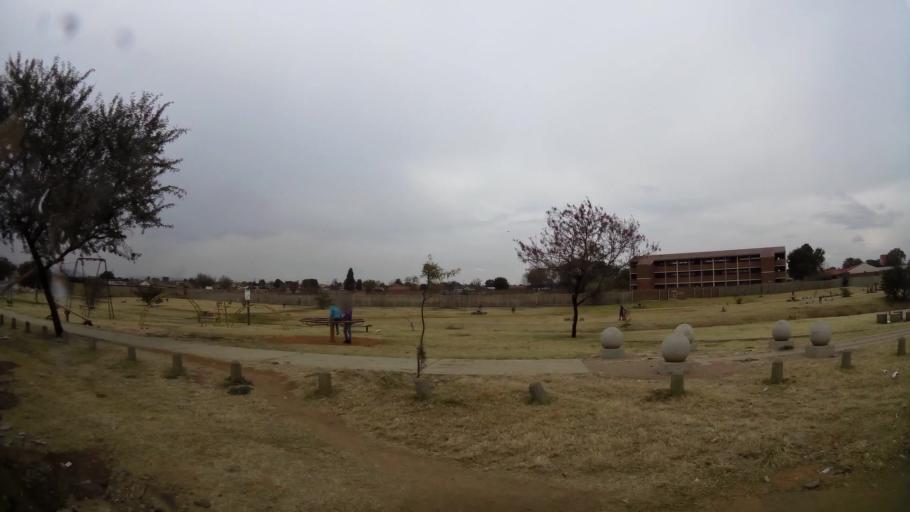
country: ZA
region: Gauteng
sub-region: City of Tshwane Metropolitan Municipality
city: Pretoria
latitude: -25.7059
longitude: 28.3525
